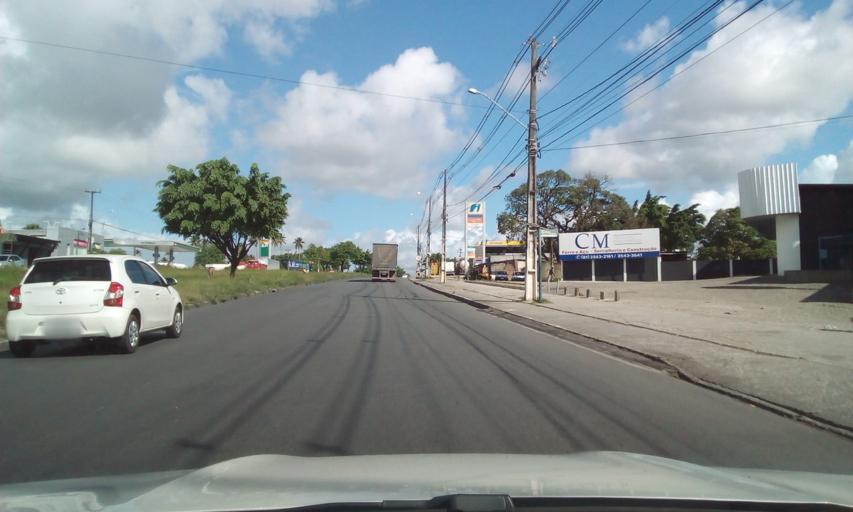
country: BR
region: Pernambuco
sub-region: Igarassu
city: Igarassu
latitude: -7.8472
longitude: -34.9101
